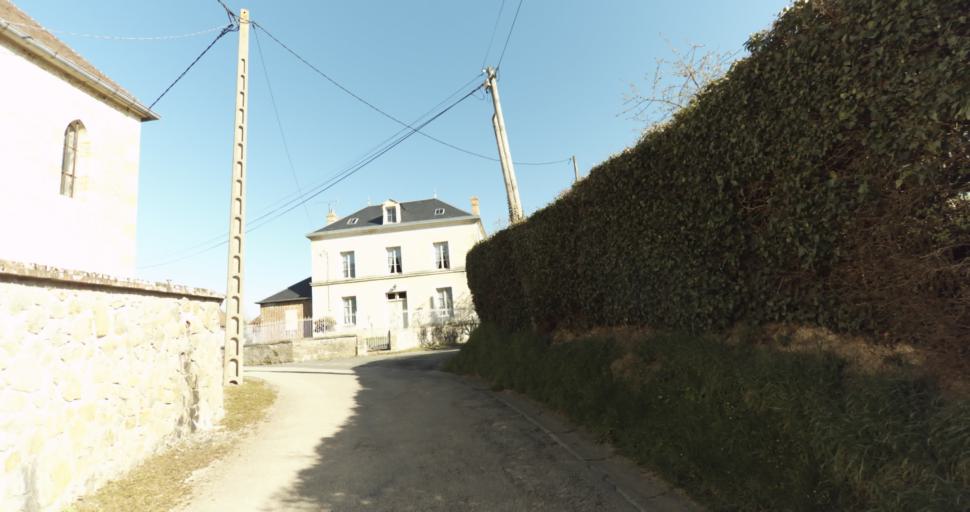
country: FR
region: Lower Normandy
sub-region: Departement de l'Orne
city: Trun
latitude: 48.9412
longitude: 0.0334
